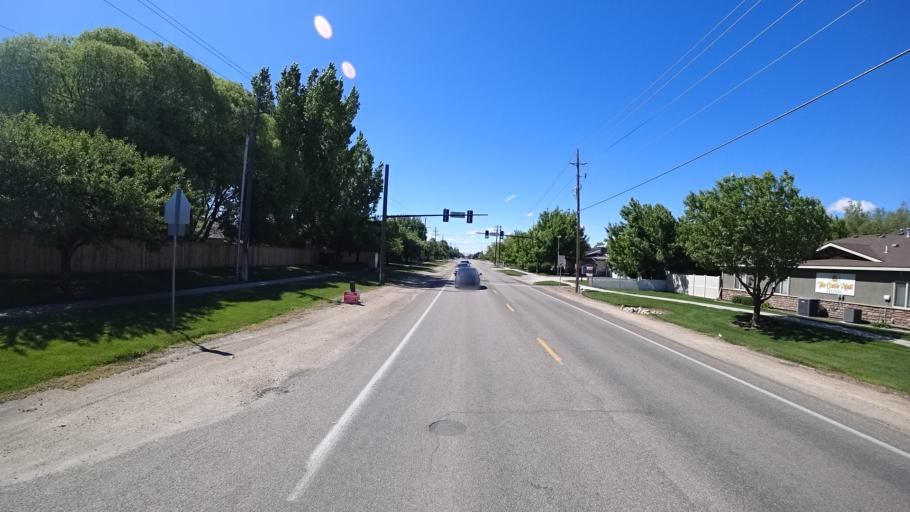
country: US
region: Idaho
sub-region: Ada County
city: Meridian
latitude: 43.6377
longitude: -116.3745
